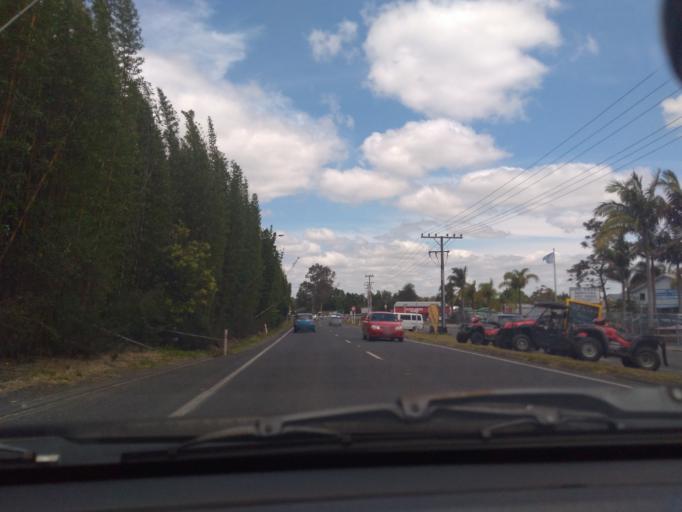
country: NZ
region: Northland
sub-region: Far North District
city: Kerikeri
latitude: -35.2072
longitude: 173.9184
